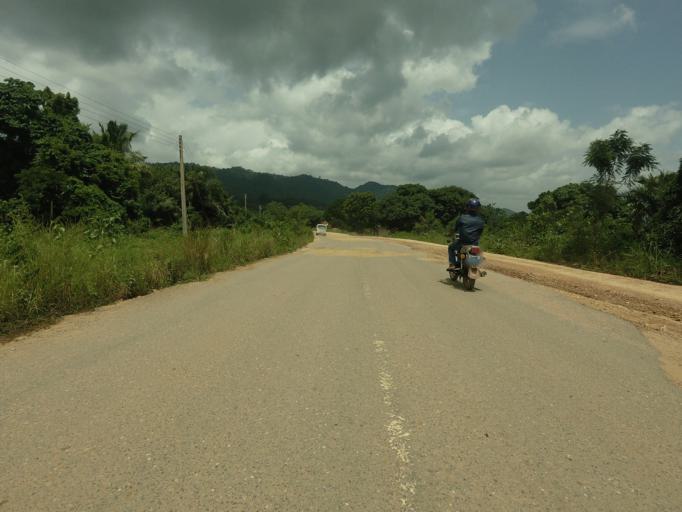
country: GH
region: Volta
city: Ho
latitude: 6.6974
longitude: 0.3351
